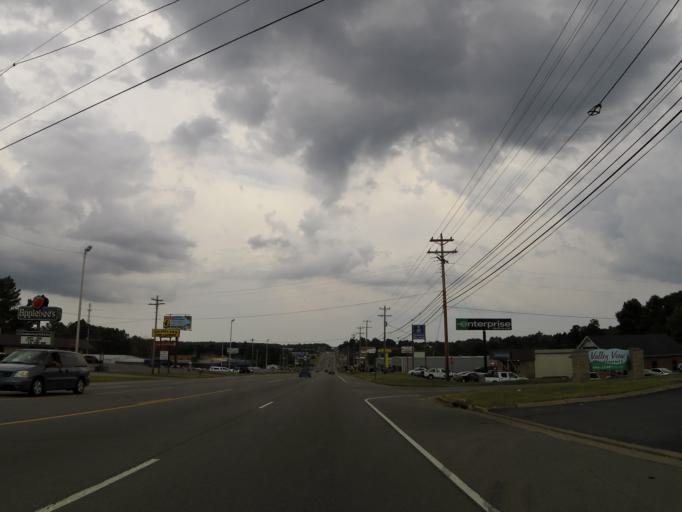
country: US
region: Tennessee
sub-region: Dickson County
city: Dickson
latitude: 36.0597
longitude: -87.3742
